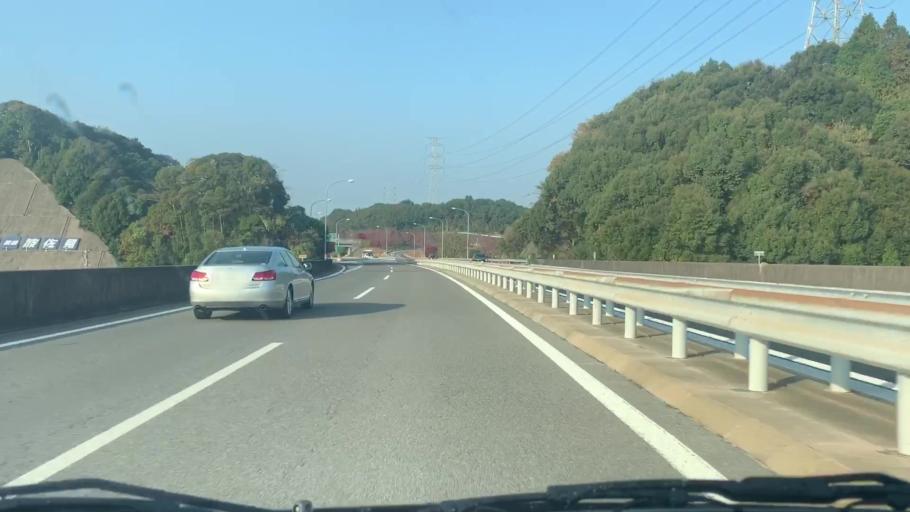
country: JP
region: Saga Prefecture
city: Ureshinomachi-shimojuku
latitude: 33.1567
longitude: 129.8965
